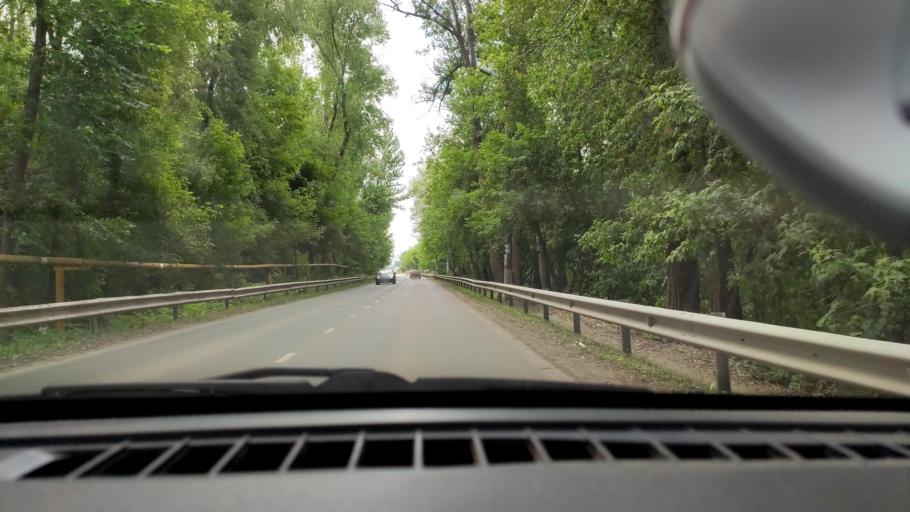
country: RU
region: Samara
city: Novokuybyshevsk
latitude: 53.1493
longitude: 49.9810
